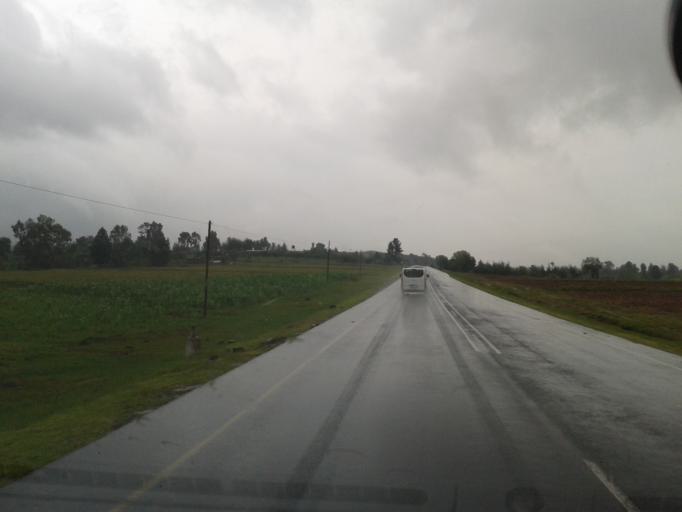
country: LS
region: Maseru
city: Nako
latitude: -29.6379
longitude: 27.4782
